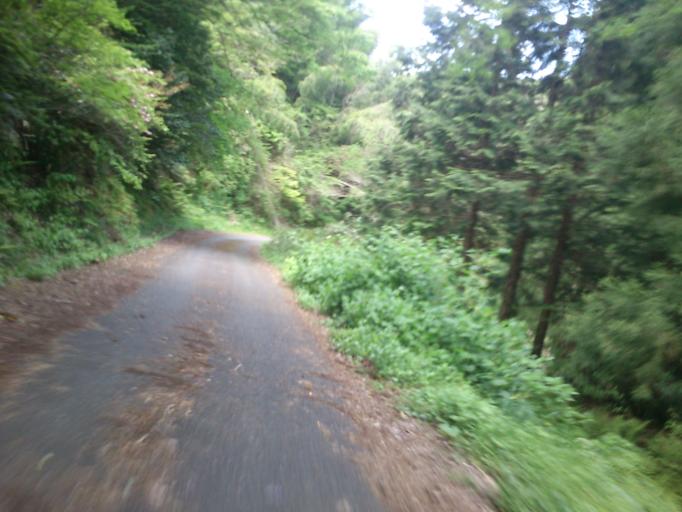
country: JP
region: Kyoto
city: Miyazu
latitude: 35.6965
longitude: 135.1354
